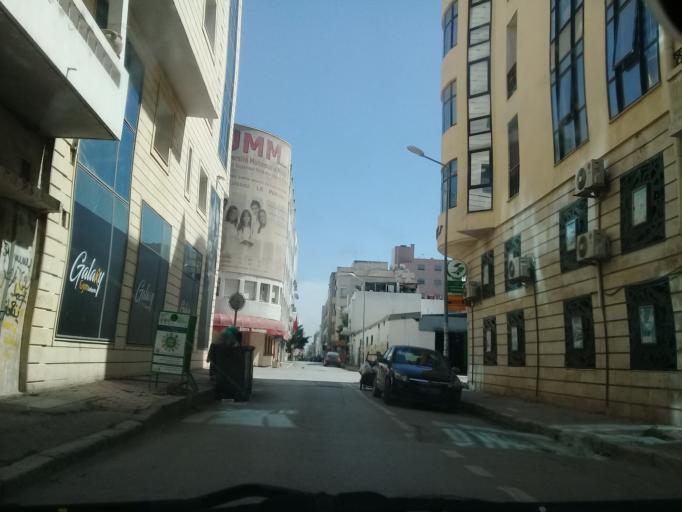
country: TN
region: Tunis
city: Tunis
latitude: 36.8146
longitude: 10.1823
